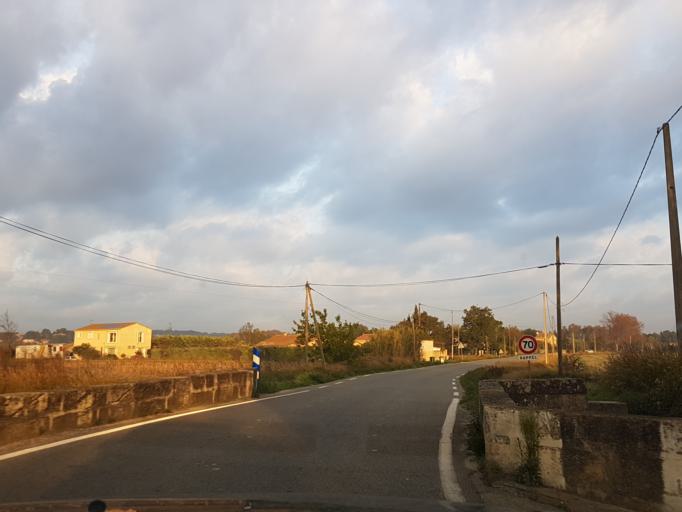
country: FR
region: Provence-Alpes-Cote d'Azur
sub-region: Departement du Vaucluse
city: Bedarrides
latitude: 44.0334
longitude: 4.9118
